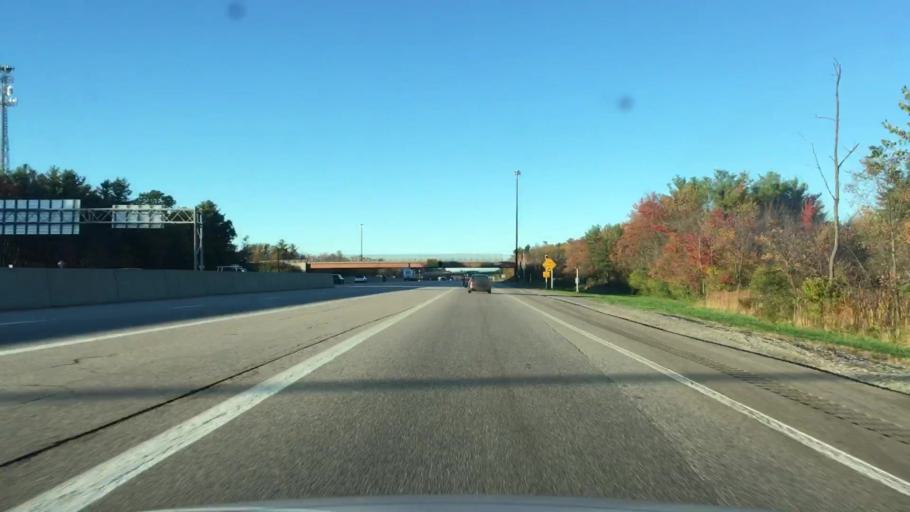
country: US
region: New Hampshire
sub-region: Rockingham County
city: North Hampton
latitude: 42.9663
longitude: -70.8552
